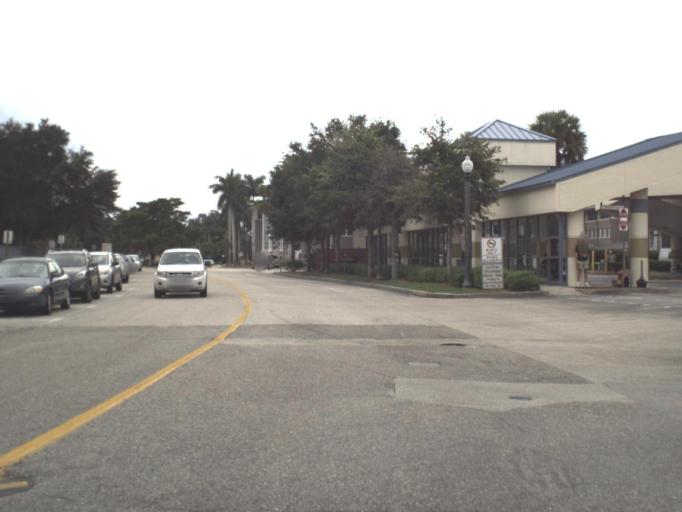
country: US
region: Florida
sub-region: Lee County
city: North Fort Myers
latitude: 26.6399
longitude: -81.8668
